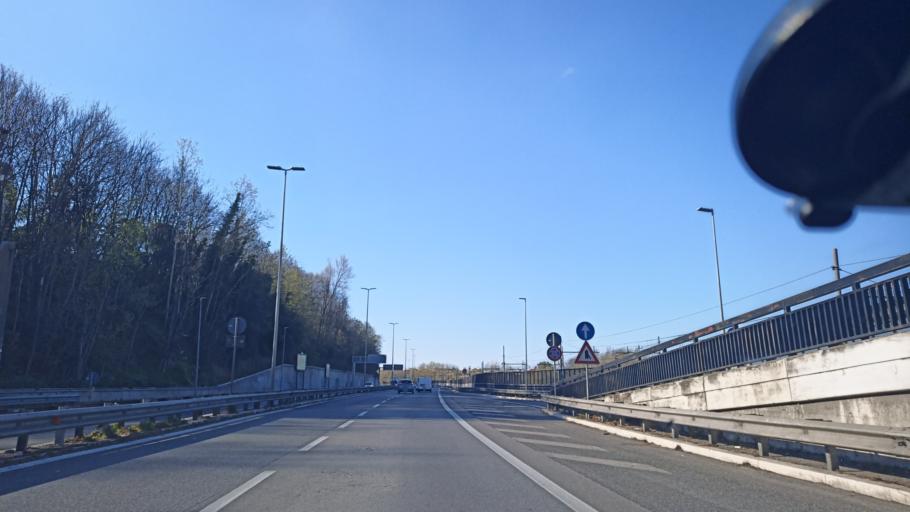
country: IT
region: Latium
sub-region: Citta metropolitana di Roma Capitale
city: Rome
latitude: 41.9348
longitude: 12.5208
